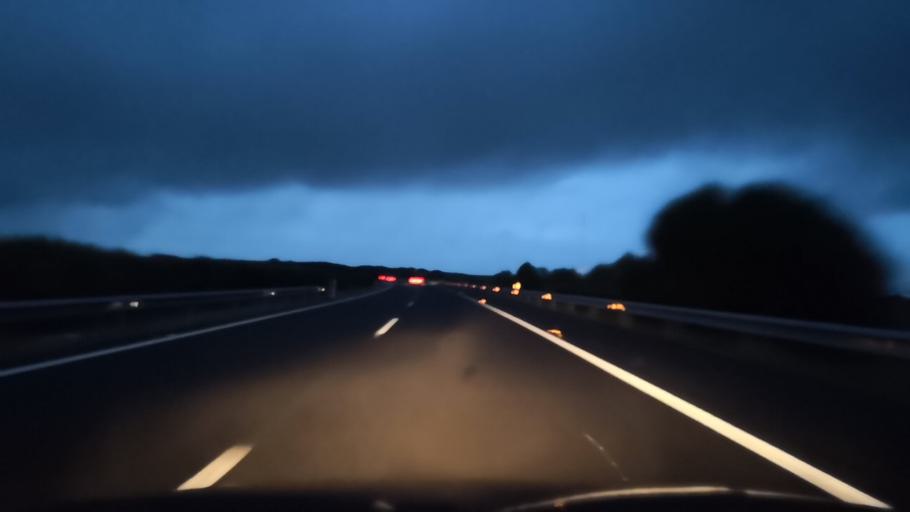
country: ES
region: Extremadura
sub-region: Provincia de Caceres
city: Aldea del Cano
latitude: 39.3344
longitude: -6.3337
